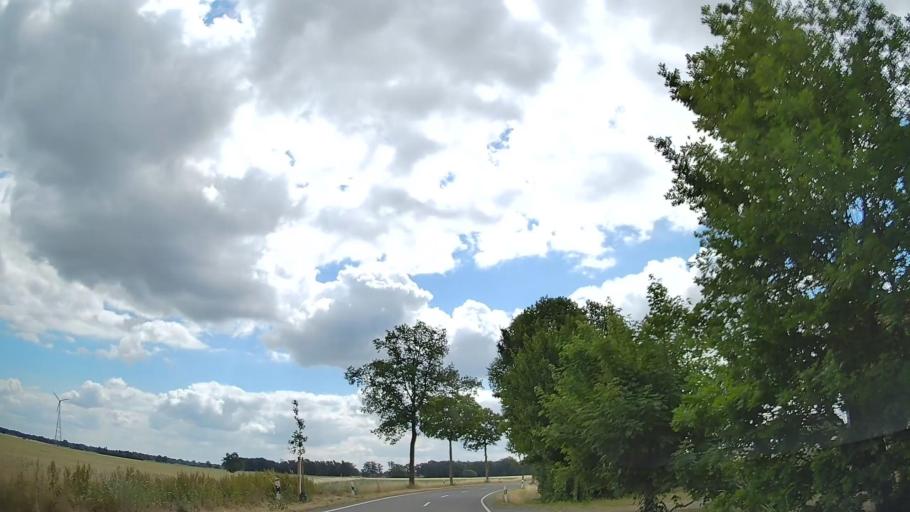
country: DE
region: Lower Saxony
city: Brockum
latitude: 52.4463
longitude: 8.5028
